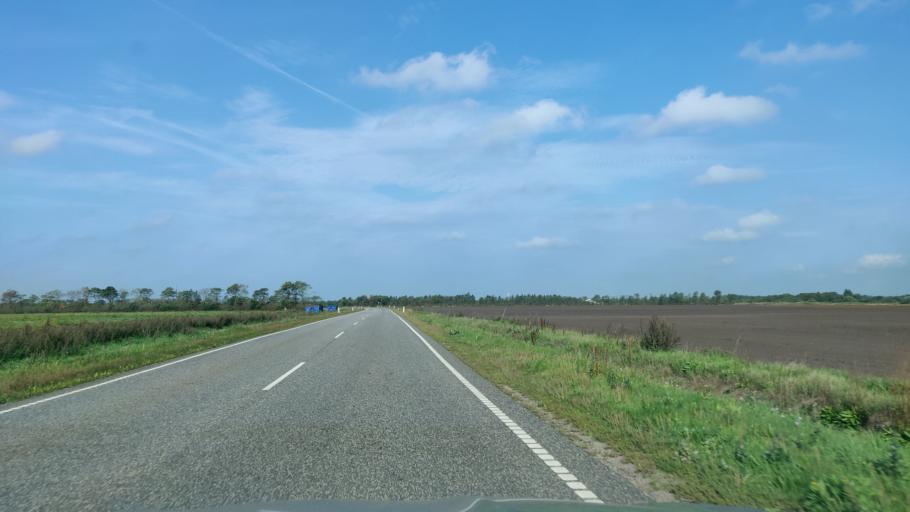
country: DK
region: Central Jutland
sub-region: Herning Kommune
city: Sunds
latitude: 56.2634
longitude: 9.0226
